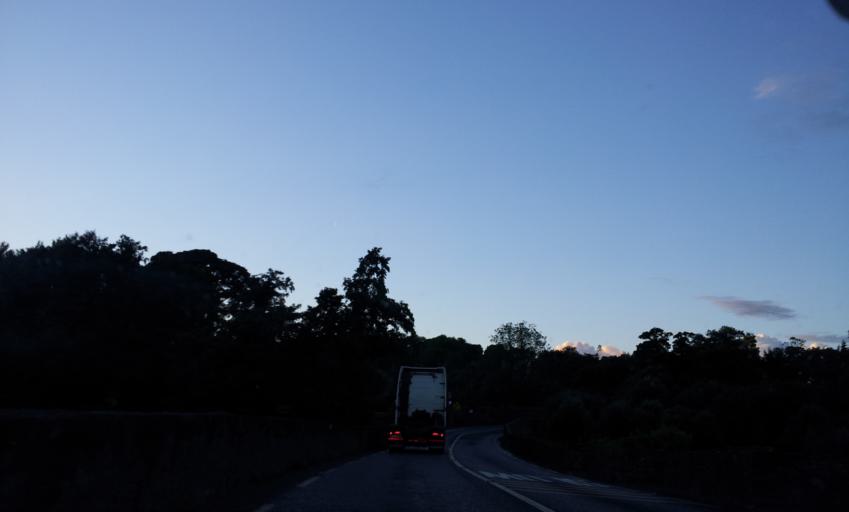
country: IE
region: Munster
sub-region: County Limerick
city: Adare
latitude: 52.5683
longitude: -8.7837
